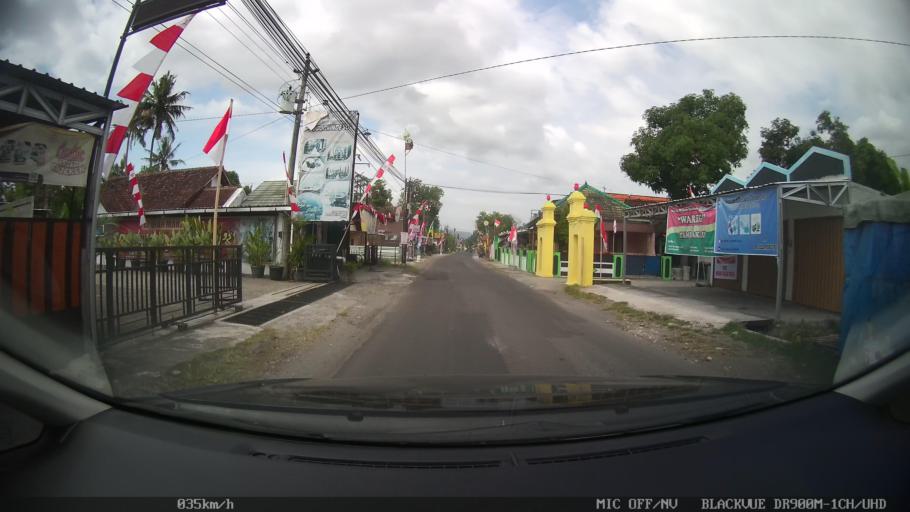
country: ID
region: Daerah Istimewa Yogyakarta
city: Depok
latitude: -7.7837
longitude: 110.4639
